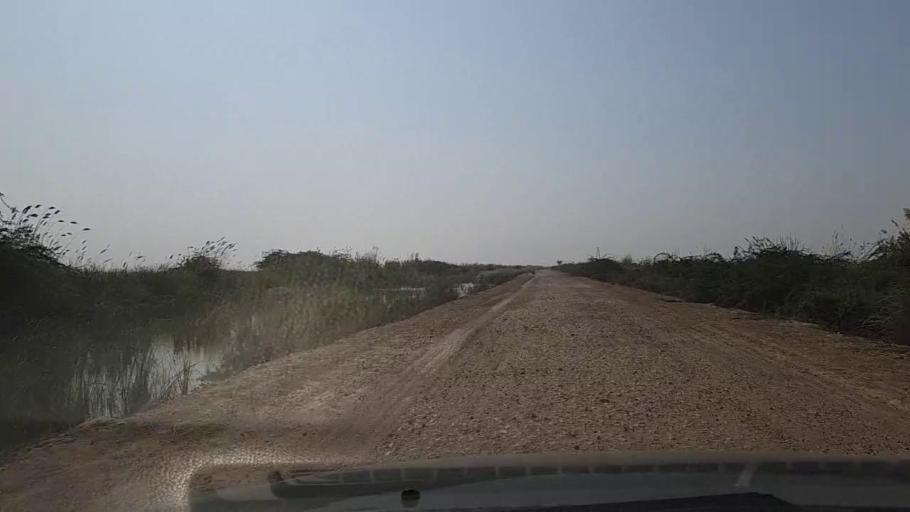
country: PK
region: Sindh
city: Mirpur Sakro
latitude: 24.3765
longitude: 67.6564
